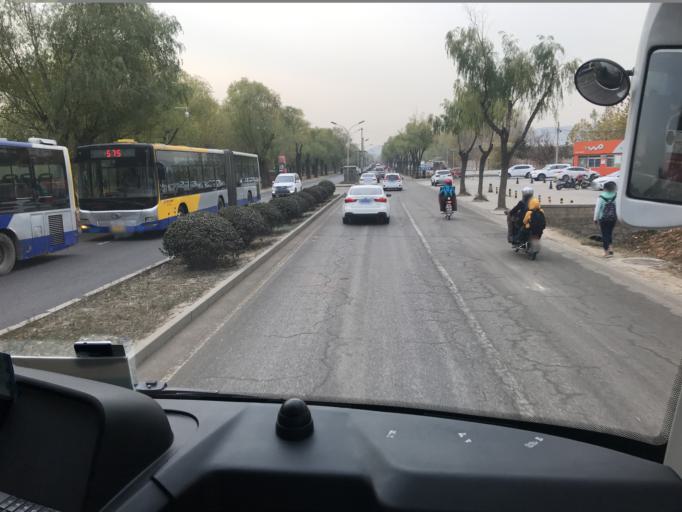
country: CN
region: Beijing
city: Wenquan
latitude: 40.0893
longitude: 116.2098
